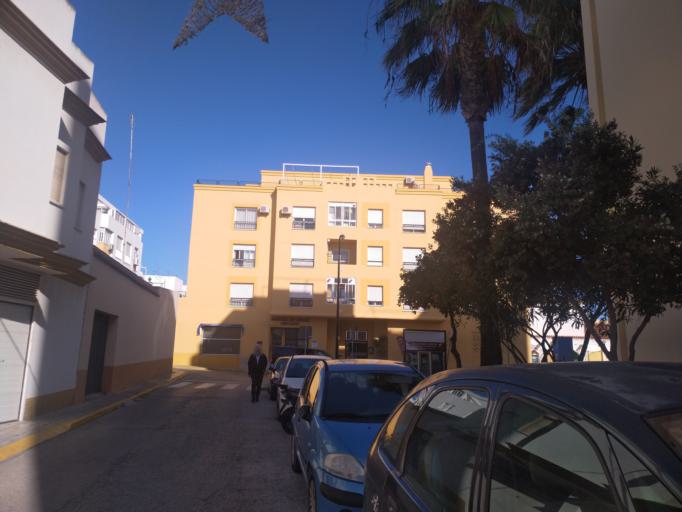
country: ES
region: Andalusia
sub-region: Provincia de Cadiz
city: San Fernando
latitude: 36.4725
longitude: -6.1941
